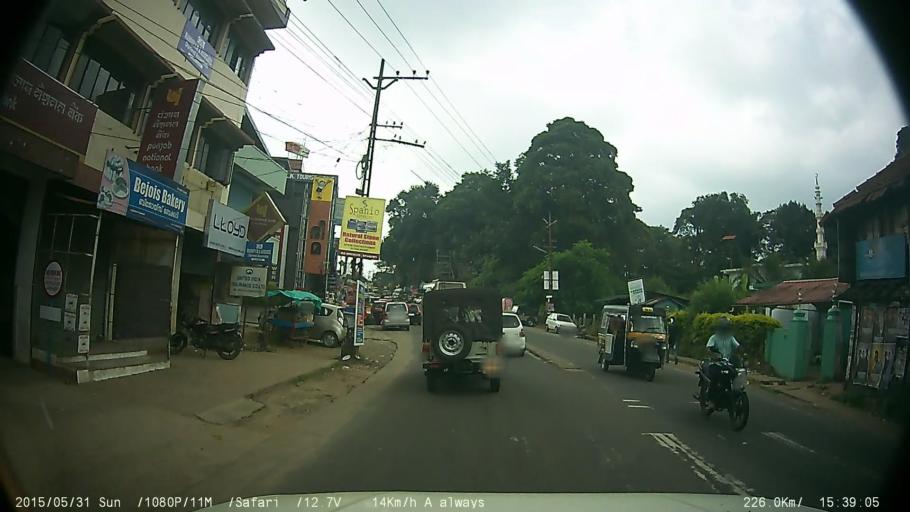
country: IN
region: Kerala
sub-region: Wayanad
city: Panamaram
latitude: 11.6641
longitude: 76.2623
